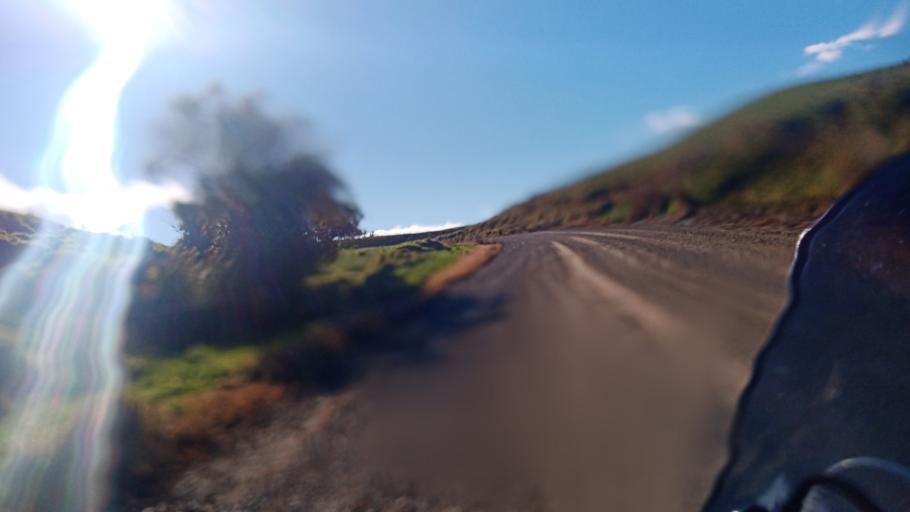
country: NZ
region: Hawke's Bay
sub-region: Wairoa District
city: Wairoa
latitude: -38.7447
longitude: 177.2811
